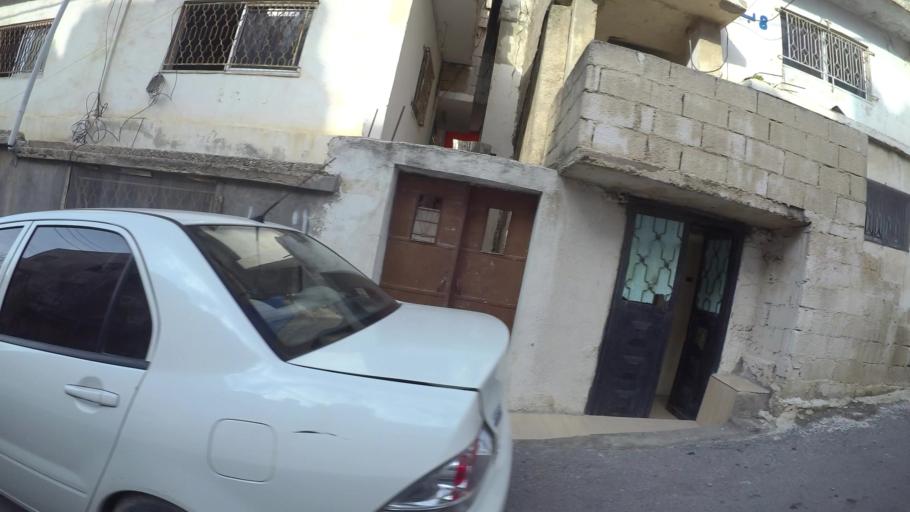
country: JO
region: Amman
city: Al Jubayhah
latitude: 32.0199
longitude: 35.8475
